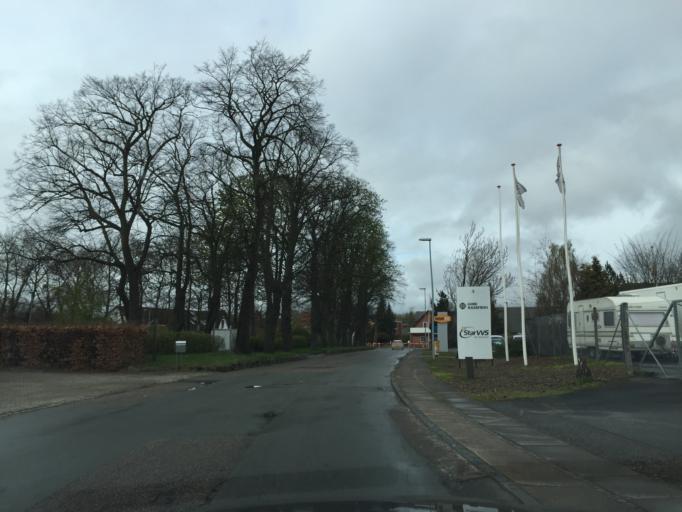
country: DK
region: South Denmark
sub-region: Odense Kommune
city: Odense
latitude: 55.3553
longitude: 10.3946
